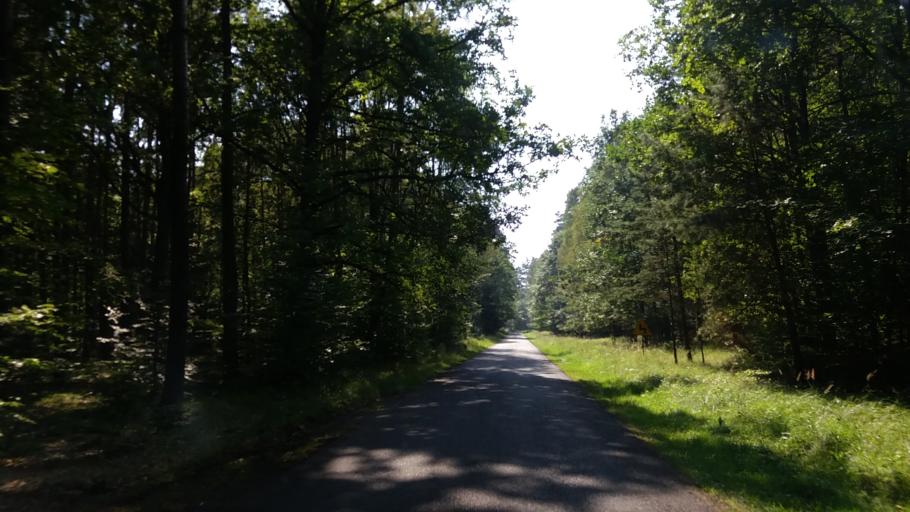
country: PL
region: West Pomeranian Voivodeship
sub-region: Powiat walecki
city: Czlopa
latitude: 53.0830
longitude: 15.9282
